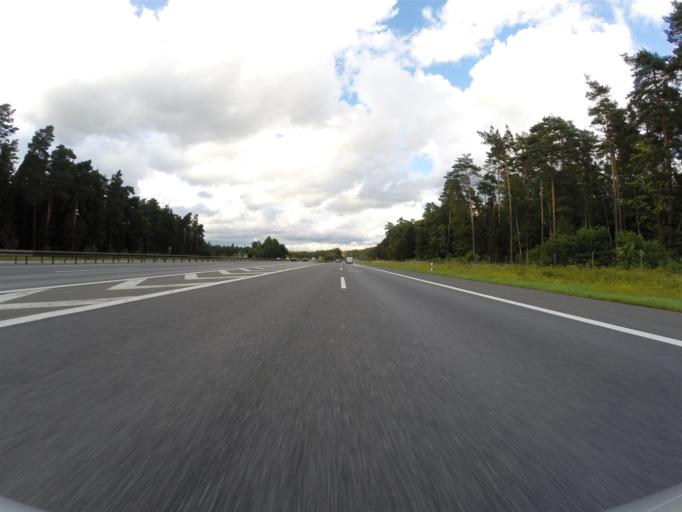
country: DE
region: Bavaria
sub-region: Regierungsbezirk Mittelfranken
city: Rothenbach an der Pegnitz
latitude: 49.4483
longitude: 11.2347
